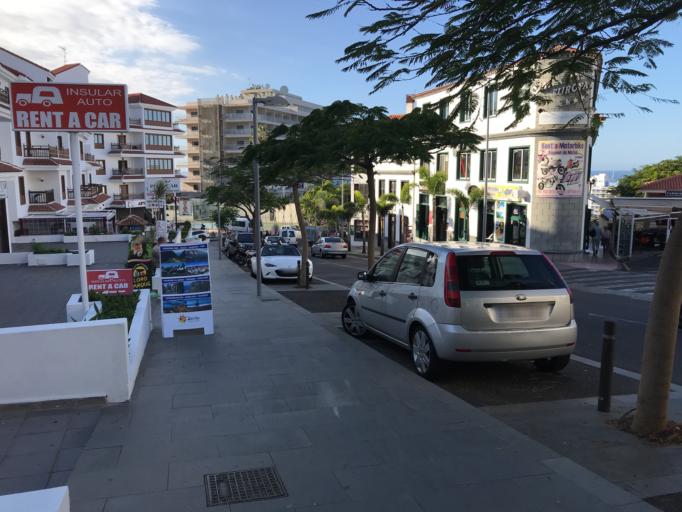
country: ES
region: Canary Islands
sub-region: Provincia de Santa Cruz de Tenerife
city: Puerto de la Cruz
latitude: 28.4138
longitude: -16.5423
